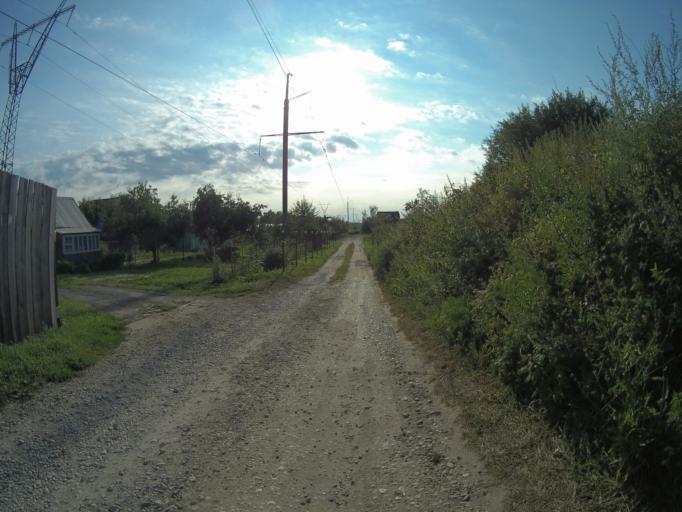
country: RU
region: Vladimir
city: Vladimir
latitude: 56.1873
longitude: 40.4236
